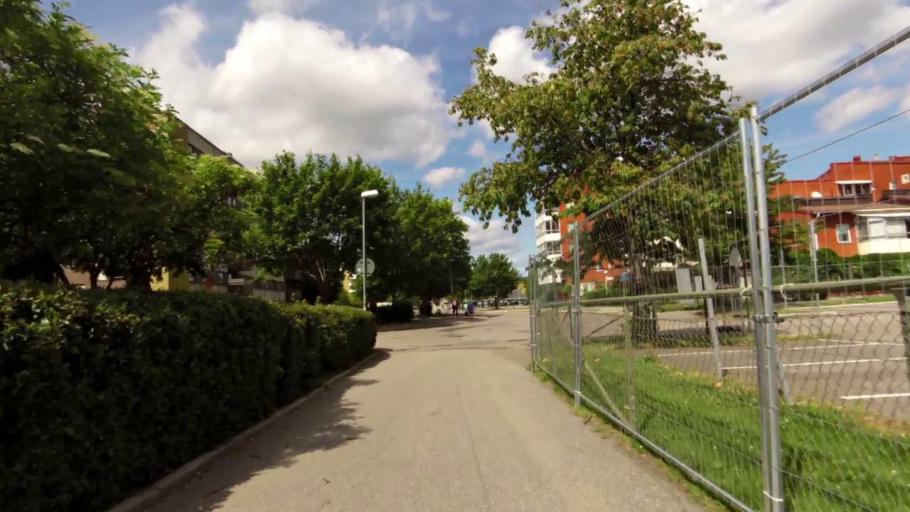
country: SE
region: OEstergoetland
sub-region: Linkopings Kommun
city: Linkoping
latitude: 58.4255
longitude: 15.5836
